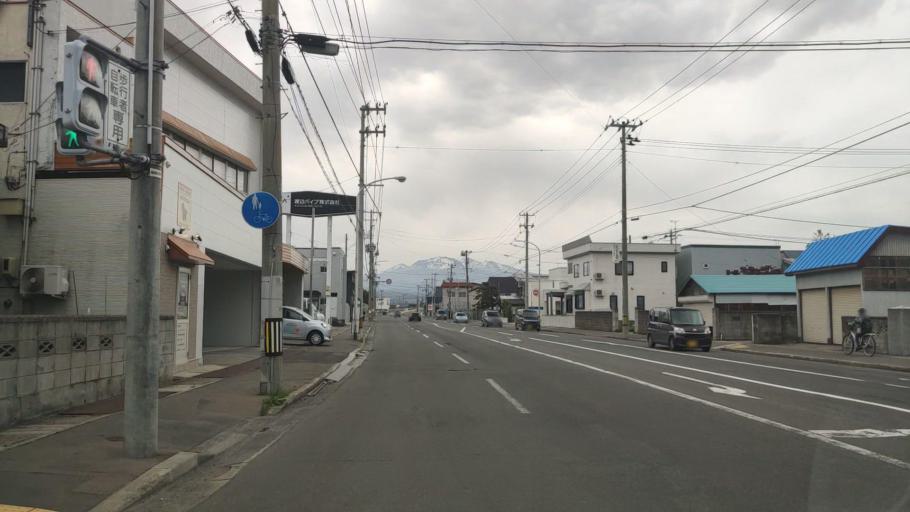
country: JP
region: Aomori
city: Aomori Shi
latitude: 40.8132
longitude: 140.7766
